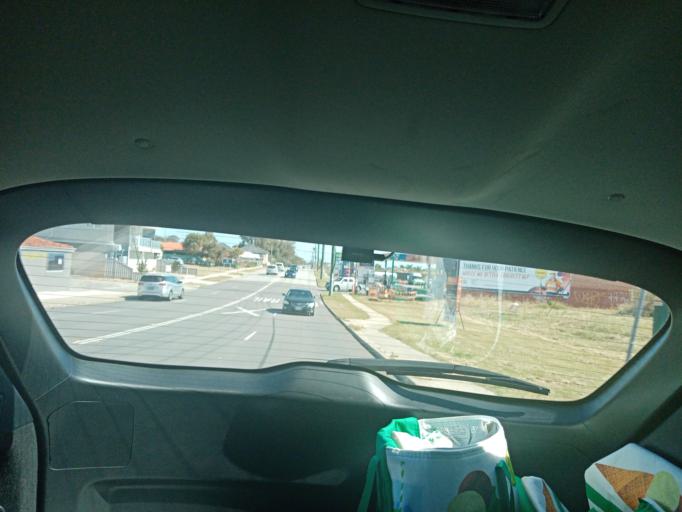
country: AU
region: Western Australia
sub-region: City of Cockburn
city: Spearwood
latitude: -32.1043
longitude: 115.7826
